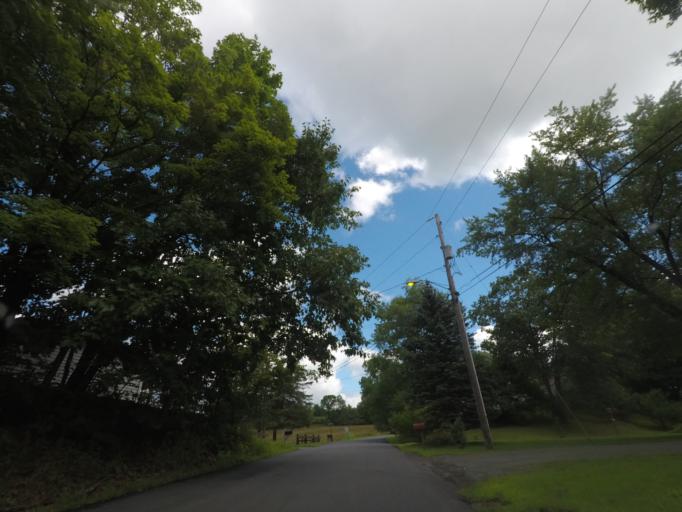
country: US
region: New York
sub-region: Rensselaer County
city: West Sand Lake
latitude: 42.6581
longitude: -73.6111
